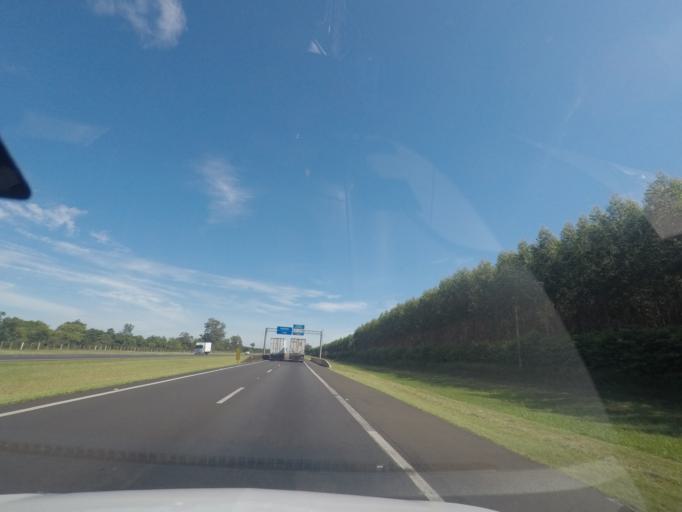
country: BR
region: Sao Paulo
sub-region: Itirapina
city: Itirapina
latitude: -22.1400
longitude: -47.8009
